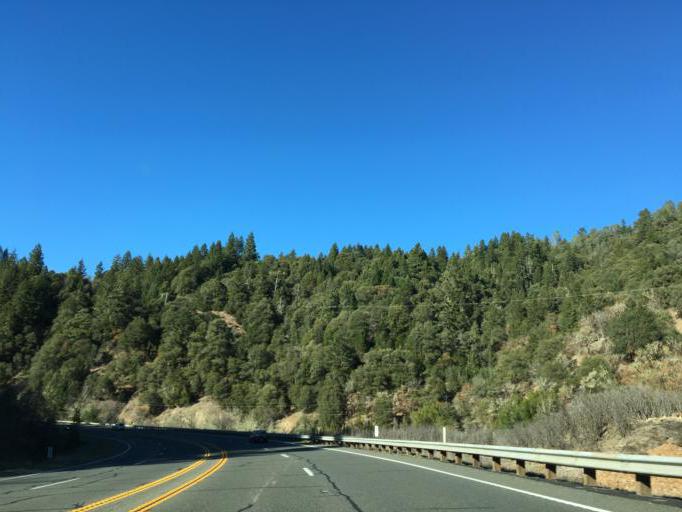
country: US
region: California
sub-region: Mendocino County
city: Brooktrails
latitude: 39.5347
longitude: -123.4044
